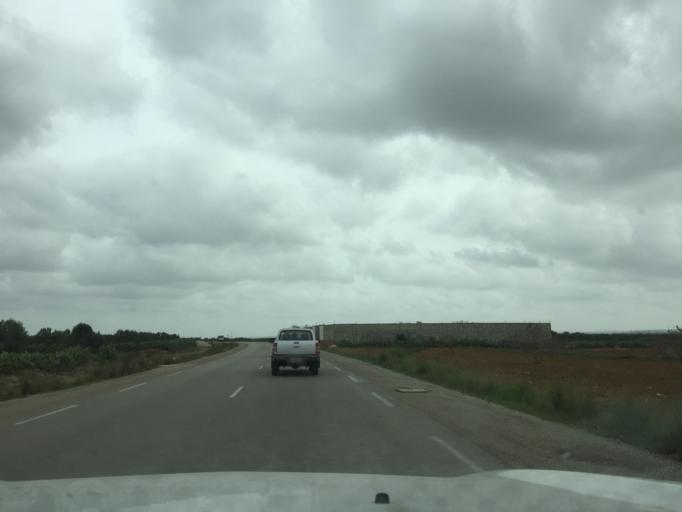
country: TN
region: Al Munastir
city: Manzil Kamil
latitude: 35.6151
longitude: 10.6719
